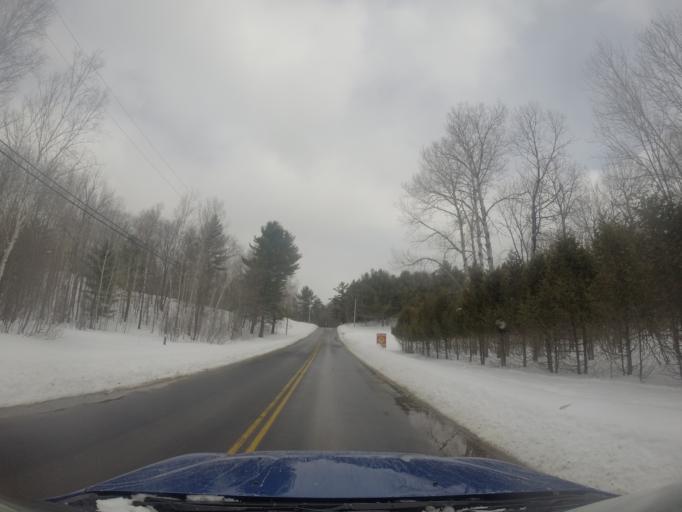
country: CA
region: Ontario
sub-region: Parry Sound District
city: Parry Sound
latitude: 45.3833
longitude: -80.0275
